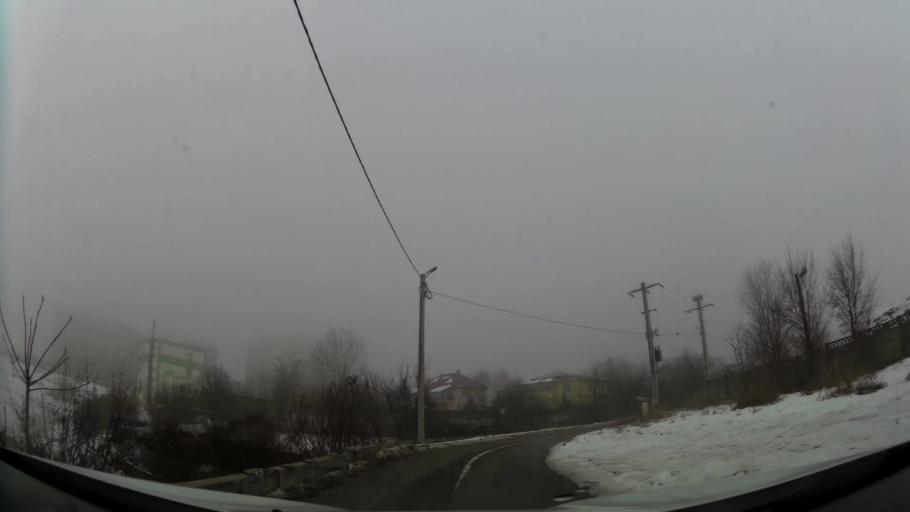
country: RO
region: Ilfov
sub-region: Comuna Chiajna
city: Rosu
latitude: 44.4486
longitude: 26.0192
